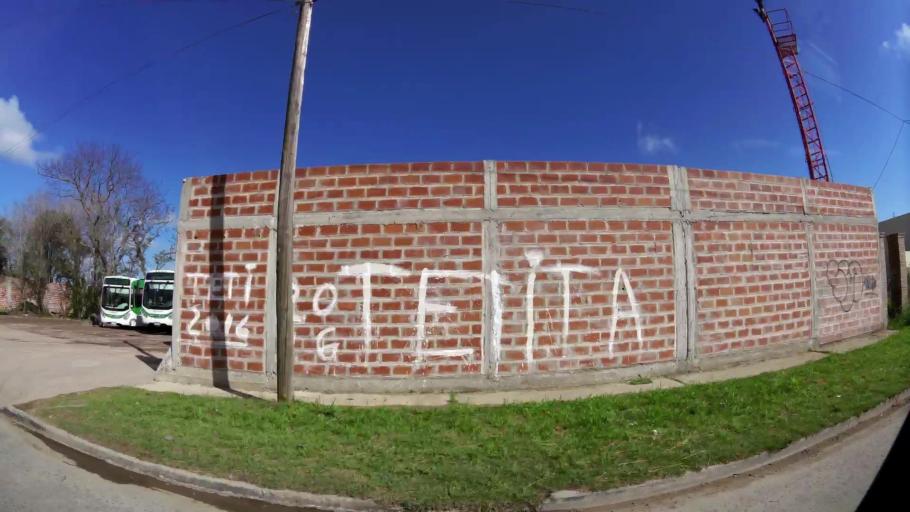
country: AR
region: Buenos Aires
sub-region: Partido de Quilmes
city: Quilmes
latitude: -34.7954
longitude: -58.1422
